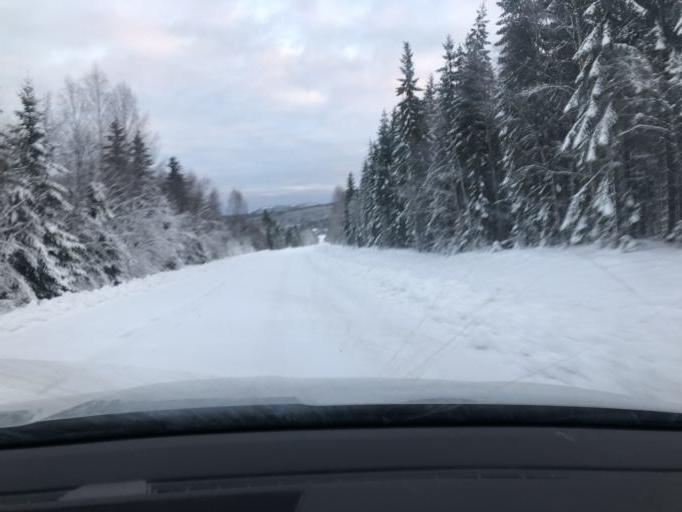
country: SE
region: Vaesternorrland
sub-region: Kramfors Kommun
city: Nordingra
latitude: 63.0031
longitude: 18.2102
